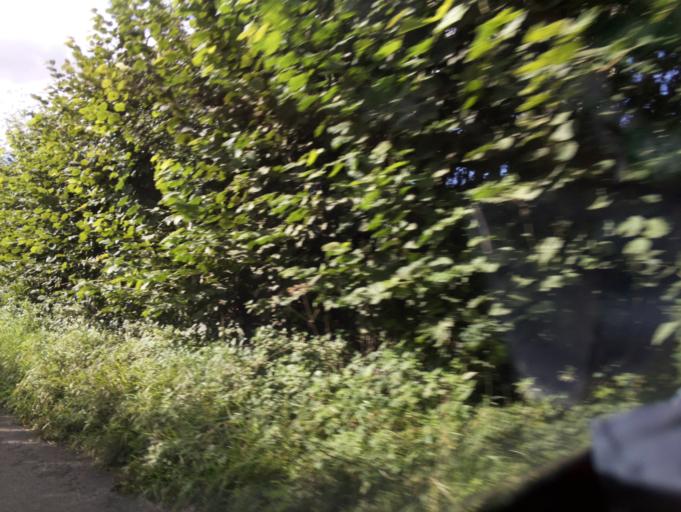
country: GB
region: England
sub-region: Hampshire
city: Chandlers Ford
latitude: 51.0529
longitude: -1.3731
